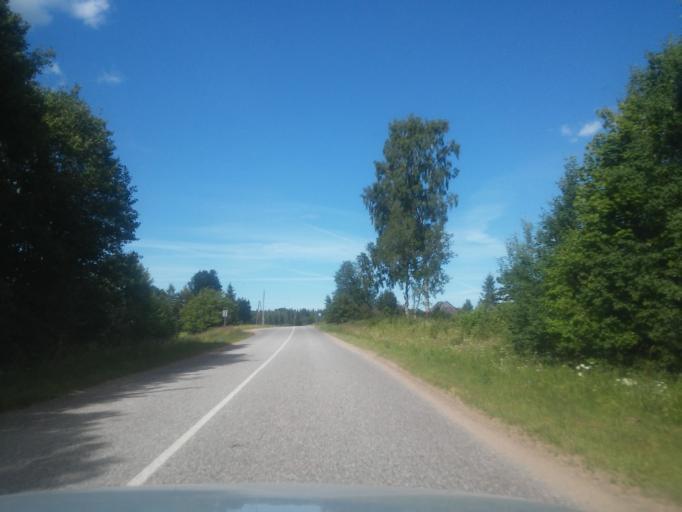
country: LV
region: Skrunda
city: Skrunda
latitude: 56.6116
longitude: 21.9457
